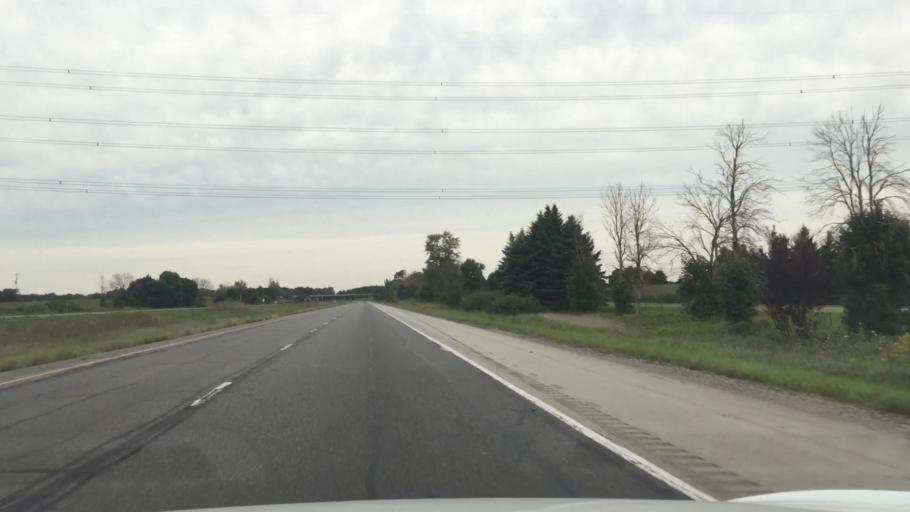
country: CA
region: Ontario
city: Delaware
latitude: 42.9580
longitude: -81.5335
